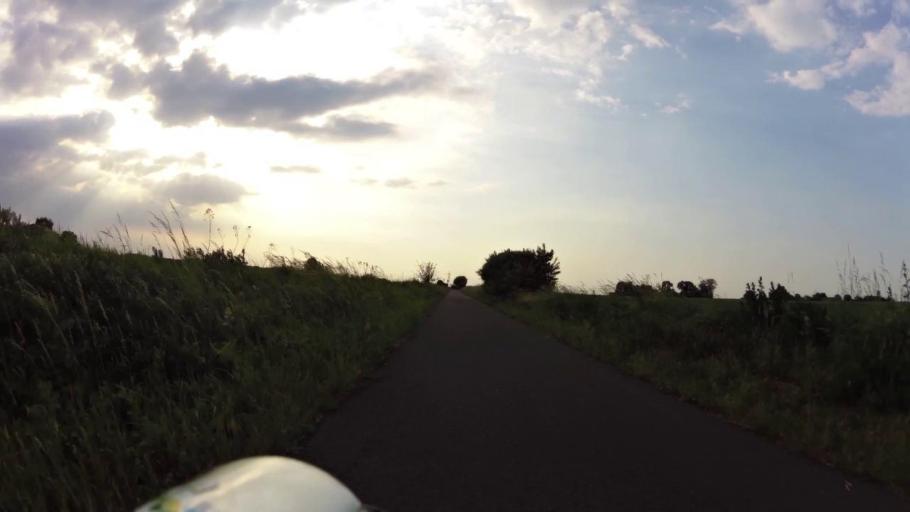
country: PL
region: Kujawsko-Pomorskie
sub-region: Powiat chelminski
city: Unislaw
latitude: 53.1761
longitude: 18.4136
